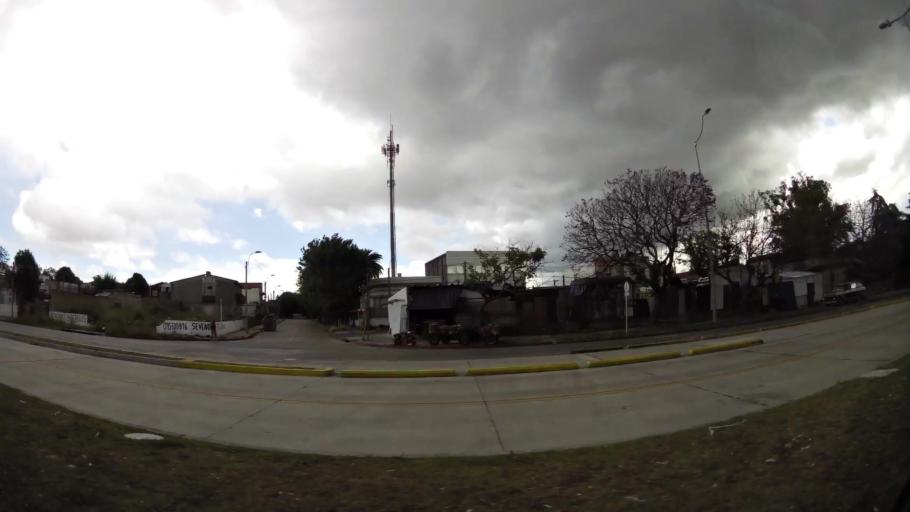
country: UY
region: Montevideo
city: Montevideo
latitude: -34.8513
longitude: -56.1594
